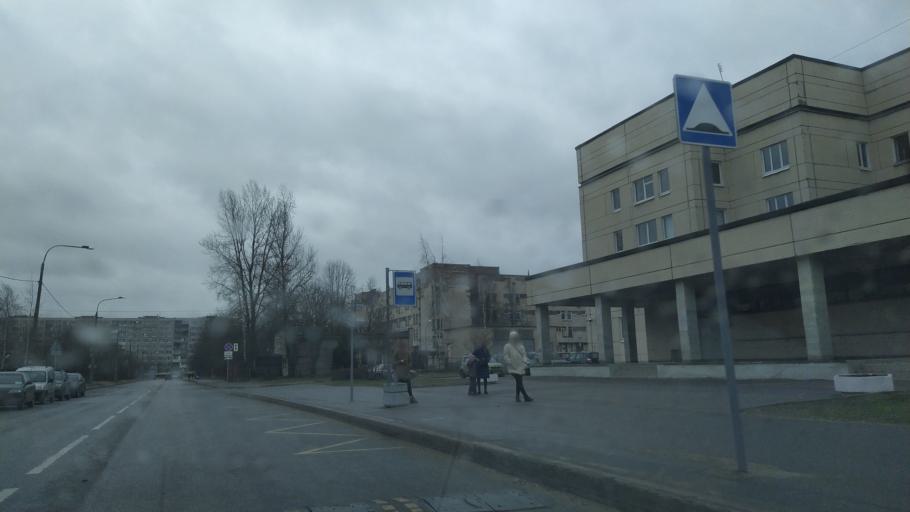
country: RU
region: Leningrad
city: Akademicheskoe
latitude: 60.0241
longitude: 30.3880
